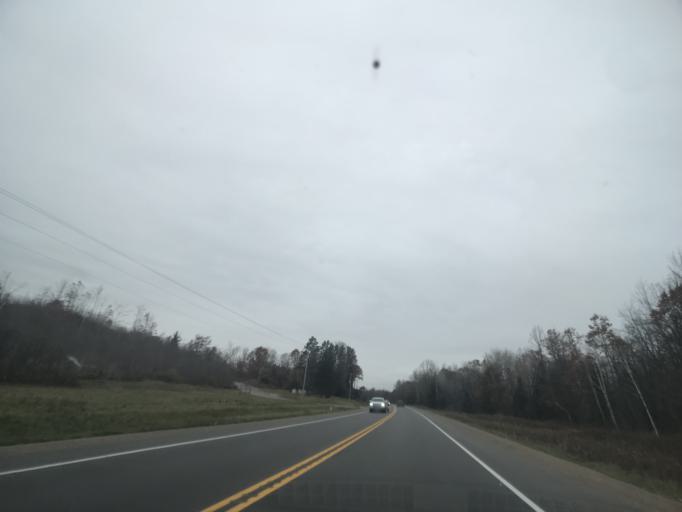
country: US
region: Wisconsin
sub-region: Menominee County
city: Legend Lake
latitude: 45.2923
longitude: -88.5115
